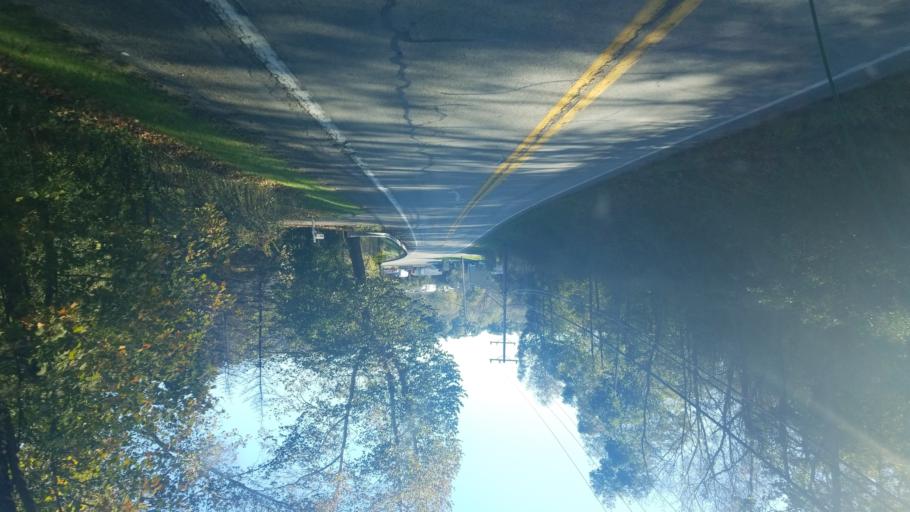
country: US
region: Pennsylvania
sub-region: Washington County
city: Burgettstown
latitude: 40.4969
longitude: -80.3599
